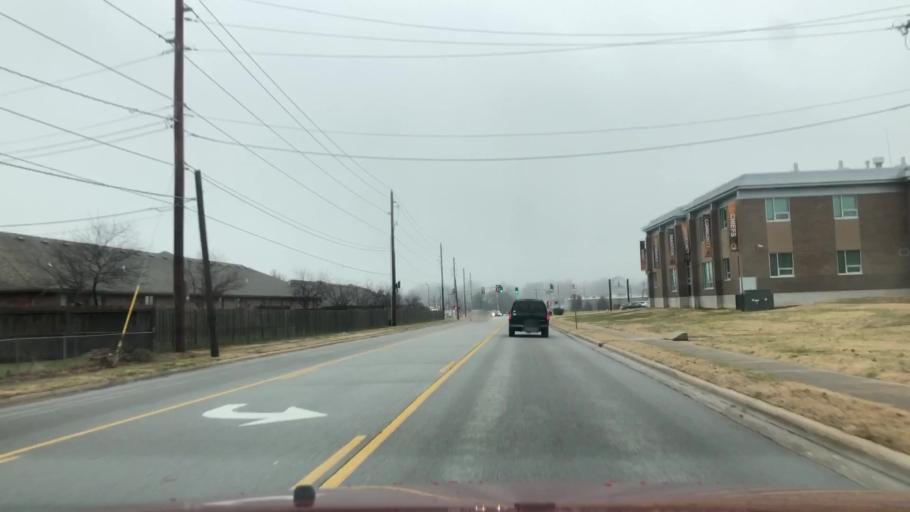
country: US
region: Missouri
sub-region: Greene County
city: Springfield
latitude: 37.1455
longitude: -93.2896
